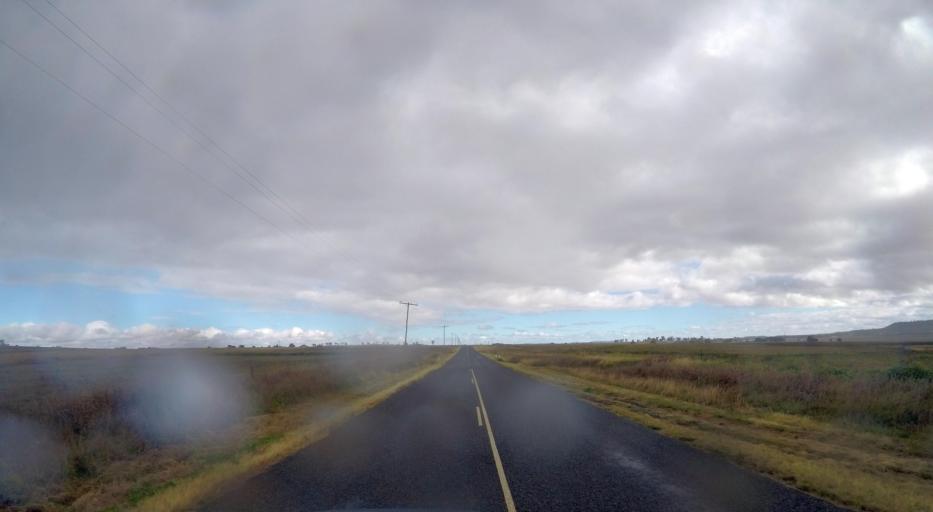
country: AU
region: Queensland
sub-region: Southern Downs
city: Warwick
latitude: -28.0521
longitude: 152.0314
